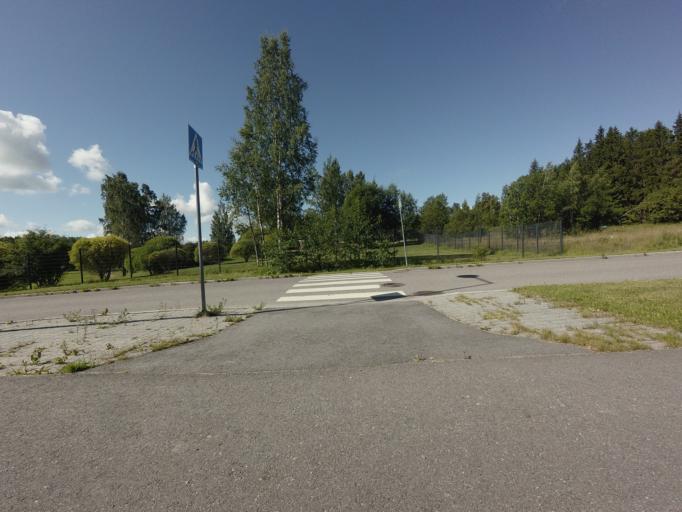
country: FI
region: Uusimaa
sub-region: Helsinki
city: Espoo
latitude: 60.1522
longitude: 24.6077
